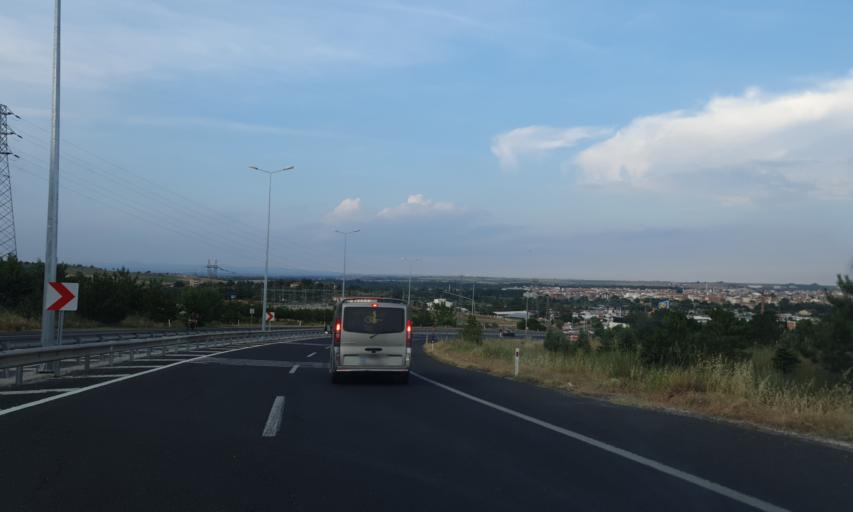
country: TR
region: Kirklareli
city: Luleburgaz
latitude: 41.4050
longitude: 27.3324
